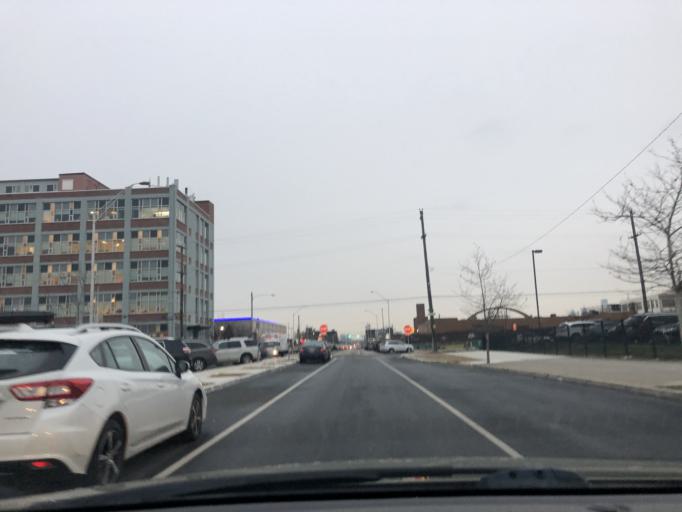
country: US
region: Pennsylvania
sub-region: Philadelphia County
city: Philadelphia
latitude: 39.9938
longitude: -75.1358
